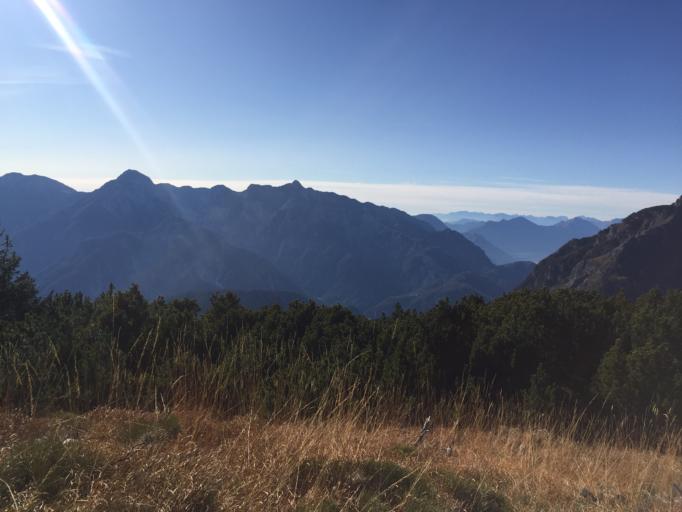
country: IT
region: Friuli Venezia Giulia
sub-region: Provincia di Udine
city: Chiusaforte
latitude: 46.4207
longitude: 13.2875
